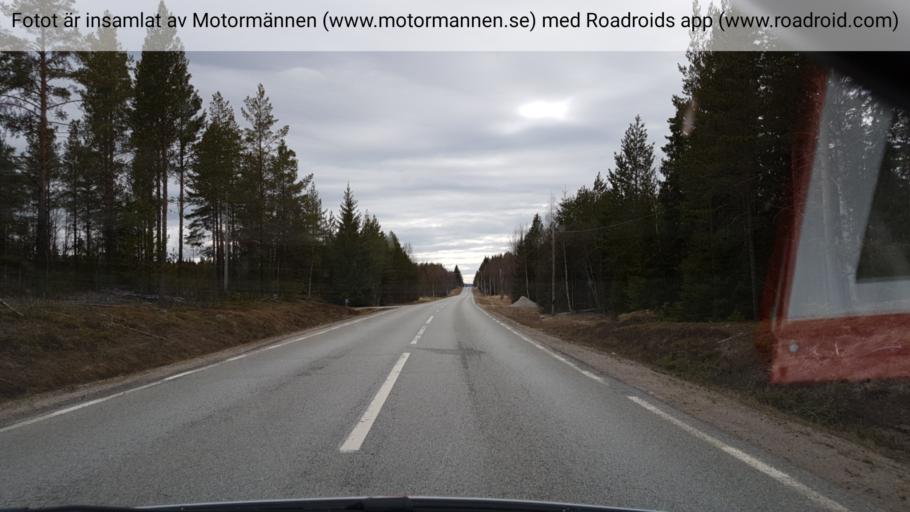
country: SE
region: Vaesterbotten
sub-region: Asele Kommun
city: Asele
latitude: 63.8730
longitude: 17.1961
